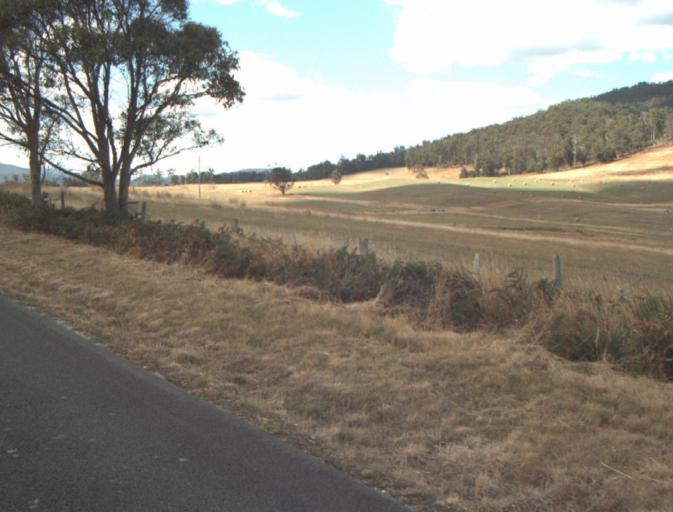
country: AU
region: Tasmania
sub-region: Launceston
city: Mayfield
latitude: -41.2023
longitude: 147.0907
